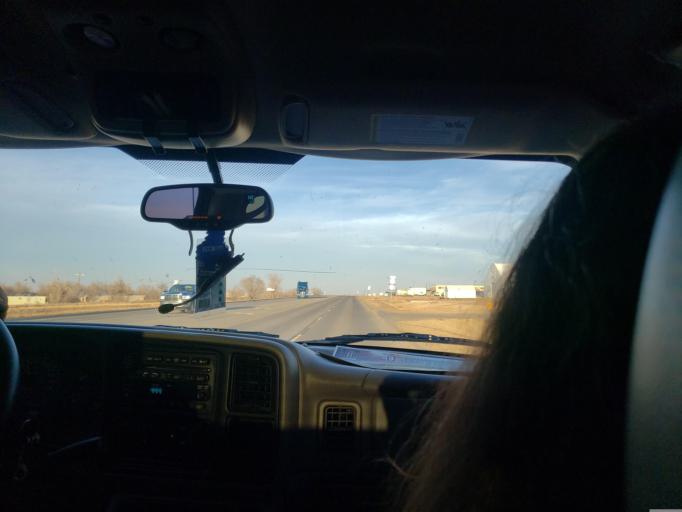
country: US
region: Oklahoma
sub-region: Texas County
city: Guymon
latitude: 36.6979
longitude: -101.4561
